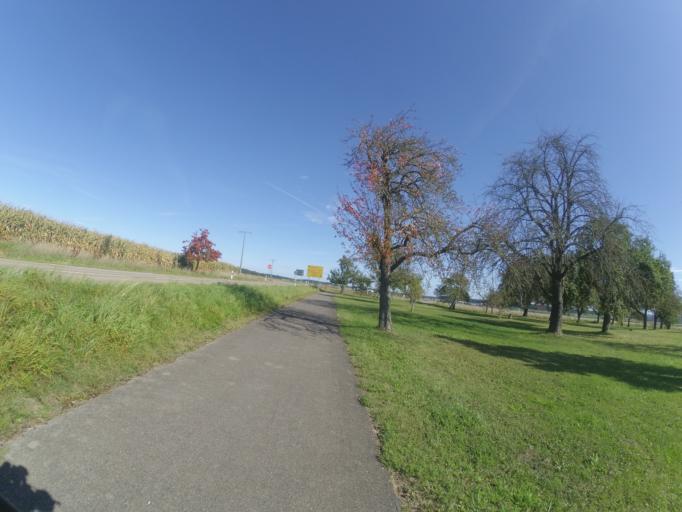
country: DE
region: Baden-Wuerttemberg
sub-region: Tuebingen Region
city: Borslingen
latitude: 48.5435
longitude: 10.0646
